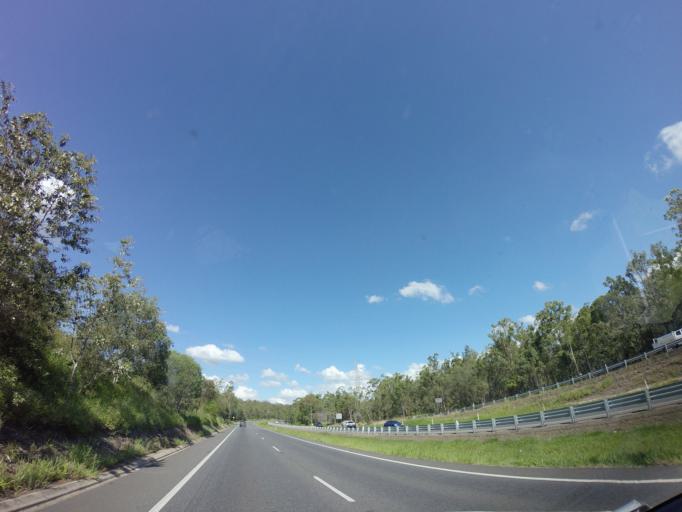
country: AU
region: Queensland
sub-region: Ipswich
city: Tivoli
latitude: -27.5743
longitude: 152.7907
